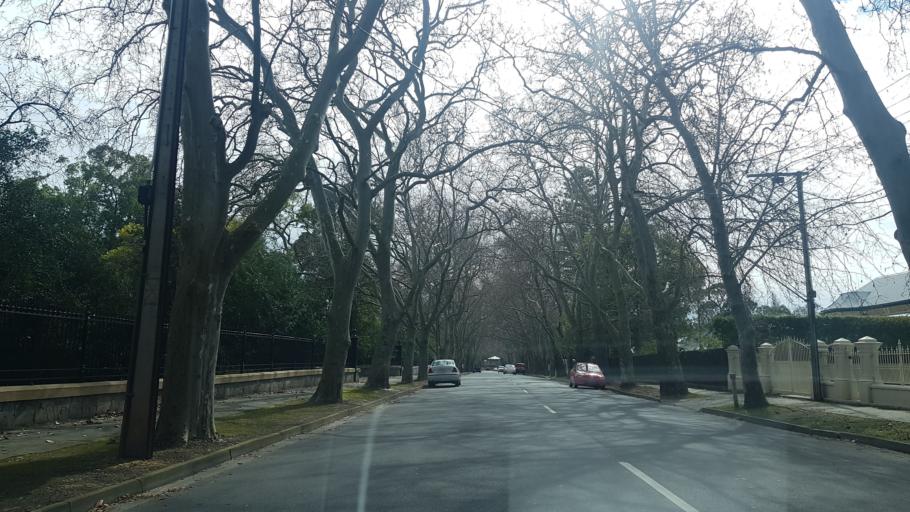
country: AU
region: South Australia
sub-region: Unley
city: Unley Park
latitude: -34.9643
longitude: 138.5987
